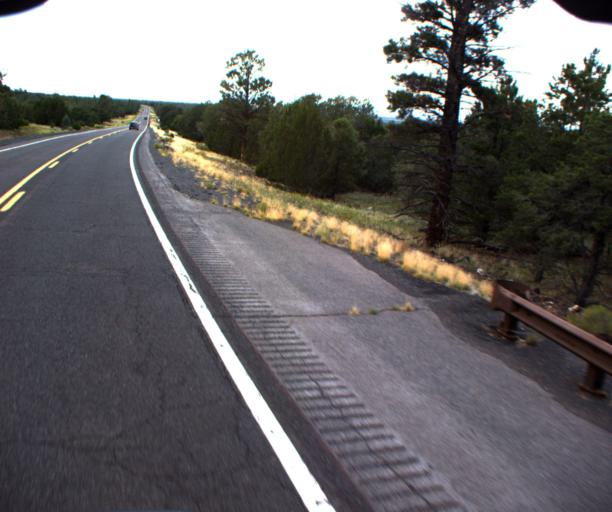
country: US
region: Arizona
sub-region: Coconino County
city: Parks
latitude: 35.5169
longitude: -111.8362
